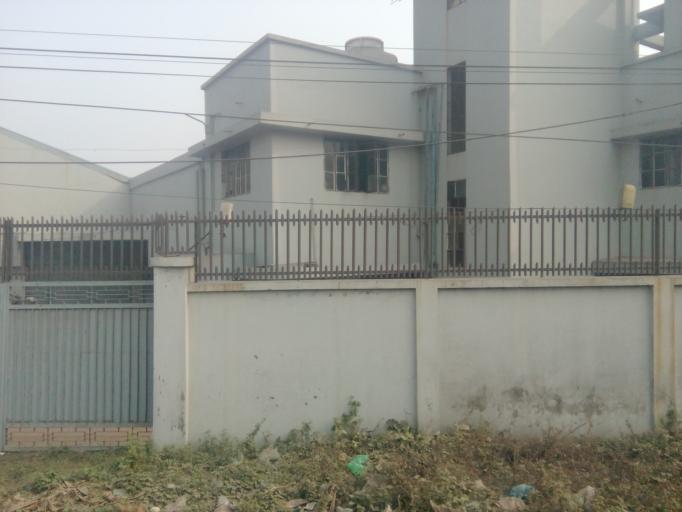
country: BD
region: Dhaka
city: Narayanganj
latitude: 23.6871
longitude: 90.5501
